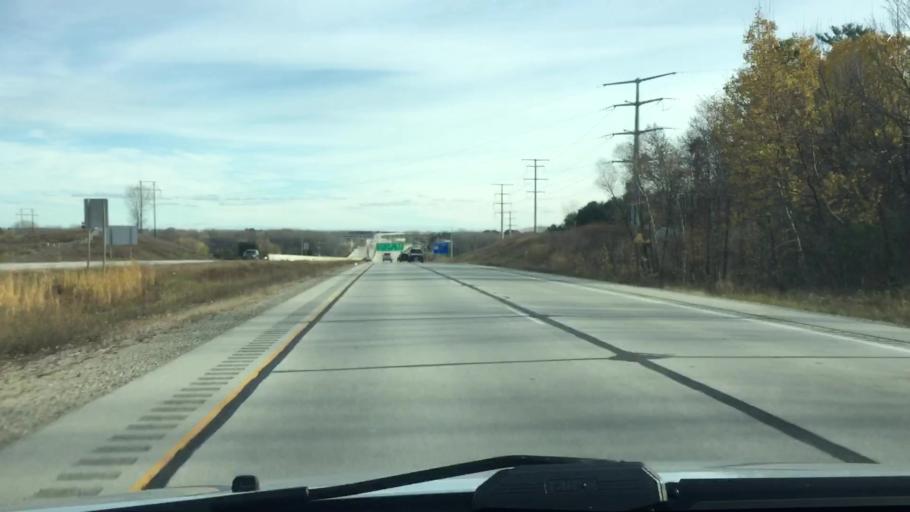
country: US
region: Wisconsin
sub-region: Brown County
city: Howard
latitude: 44.5500
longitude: -88.1054
